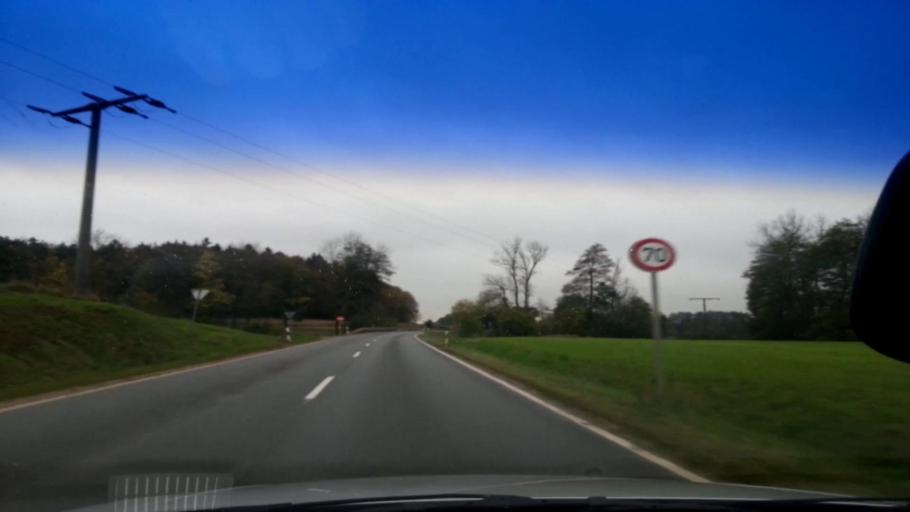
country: DE
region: Bavaria
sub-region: Upper Franconia
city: Schesslitz
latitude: 50.0034
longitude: 11.0658
